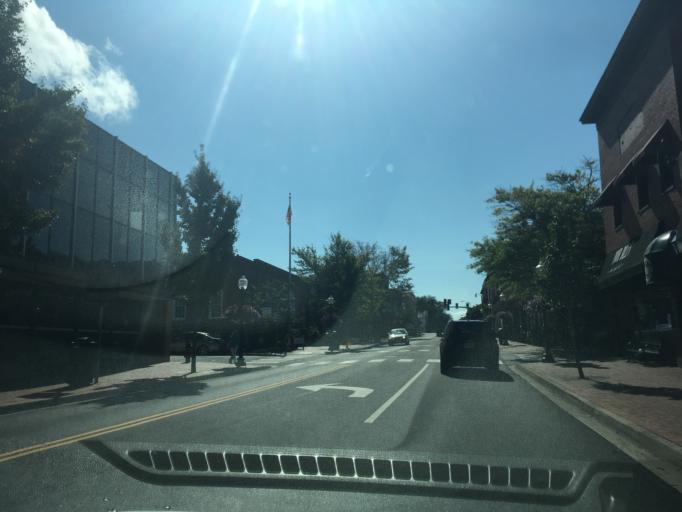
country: US
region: Virginia
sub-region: Montgomery County
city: Blacksburg
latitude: 37.2303
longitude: -80.4150
